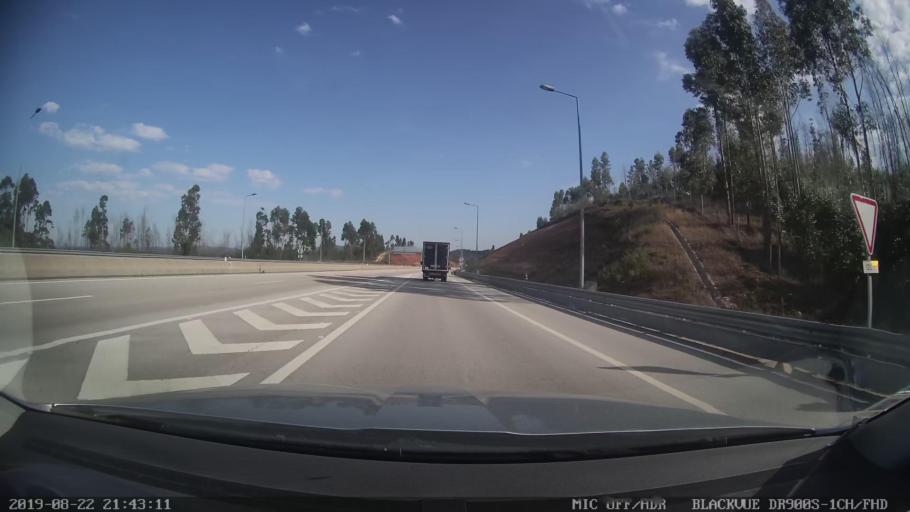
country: PT
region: Leiria
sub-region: Figueiro Dos Vinhos
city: Figueiro dos Vinhos
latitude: 39.9294
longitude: -8.3454
